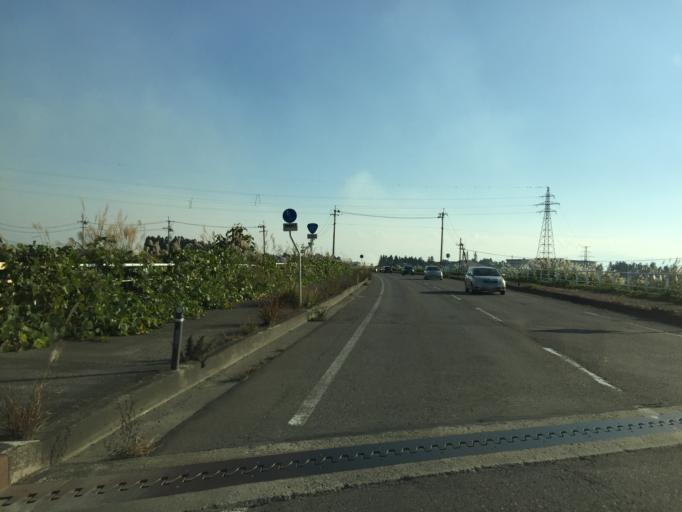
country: JP
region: Fukushima
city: Kitakata
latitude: 37.6772
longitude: 139.8880
